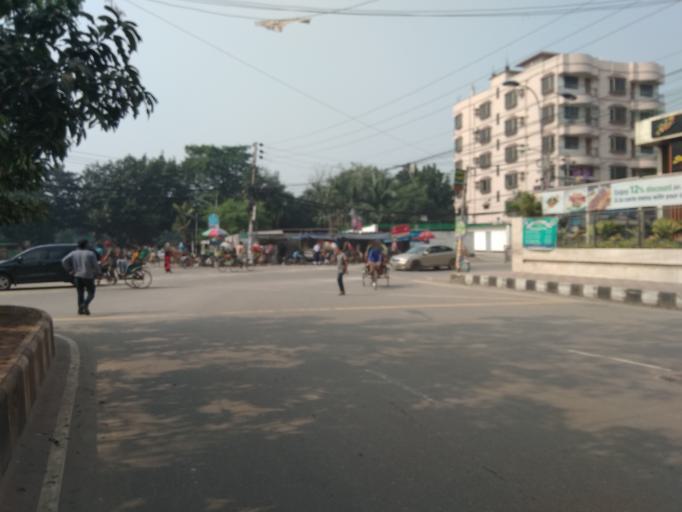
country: BD
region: Dhaka
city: Tungi
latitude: 23.8674
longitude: 90.3941
